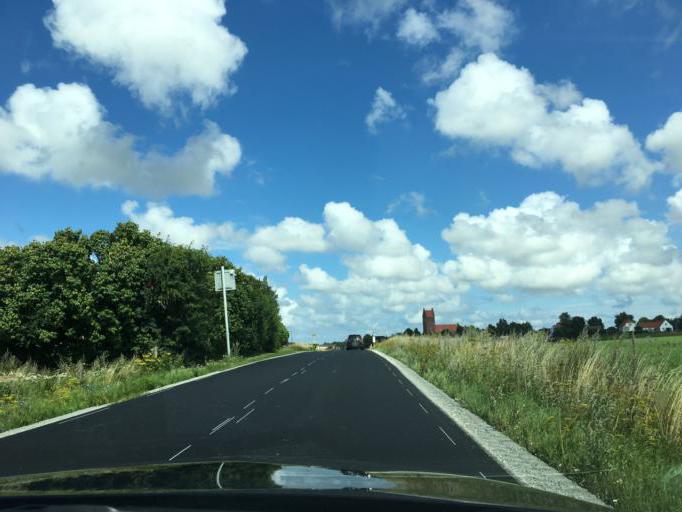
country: DK
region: Capital Region
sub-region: Gribskov Kommune
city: Helsinge
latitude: 56.0530
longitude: 12.1986
